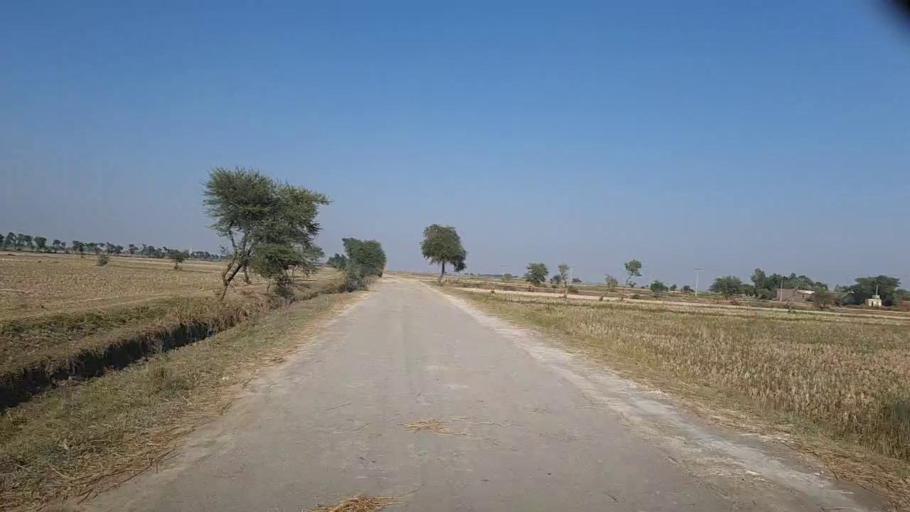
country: PK
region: Sindh
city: Thul
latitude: 28.3557
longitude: 68.7651
